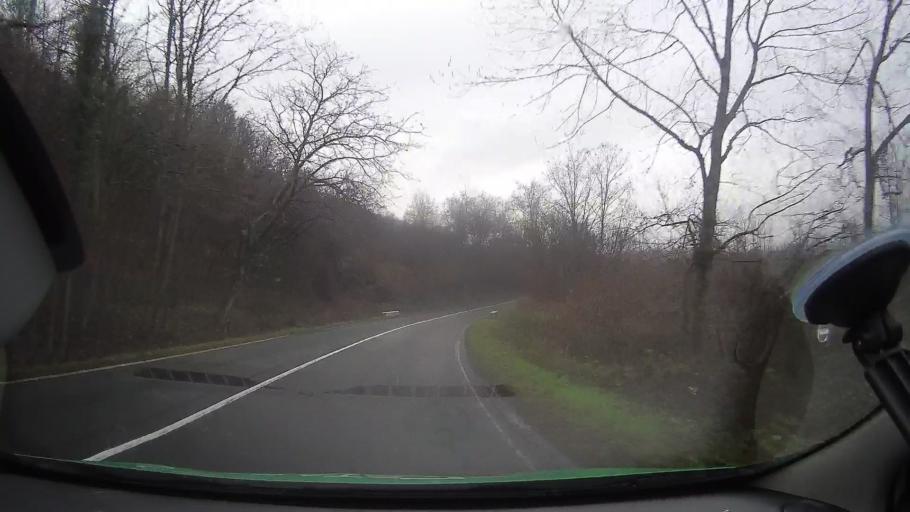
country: RO
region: Arad
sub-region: Comuna Gurahont
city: Gurahont
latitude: 46.2811
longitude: 22.3757
